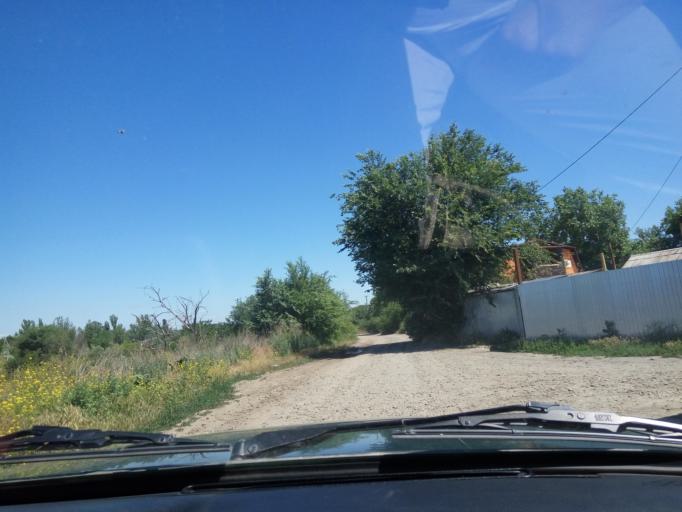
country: RU
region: Rostov
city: Bataysk
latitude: 47.0820
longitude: 39.7481
